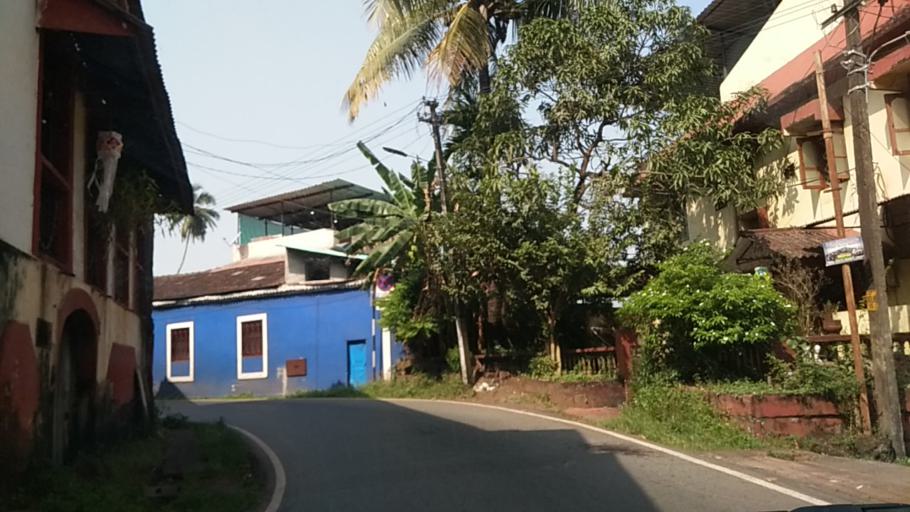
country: IN
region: Goa
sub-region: North Goa
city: Panaji
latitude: 15.5055
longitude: 73.8643
